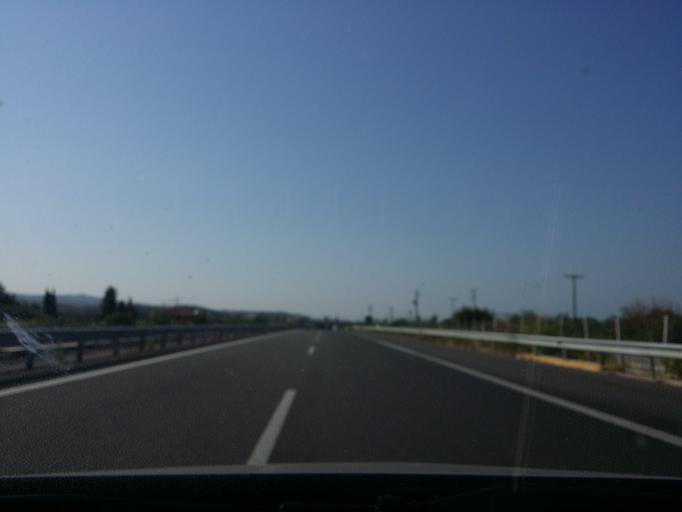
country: GR
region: Peloponnese
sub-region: Nomos Korinthias
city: Velo
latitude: 37.9559
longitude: 22.7517
